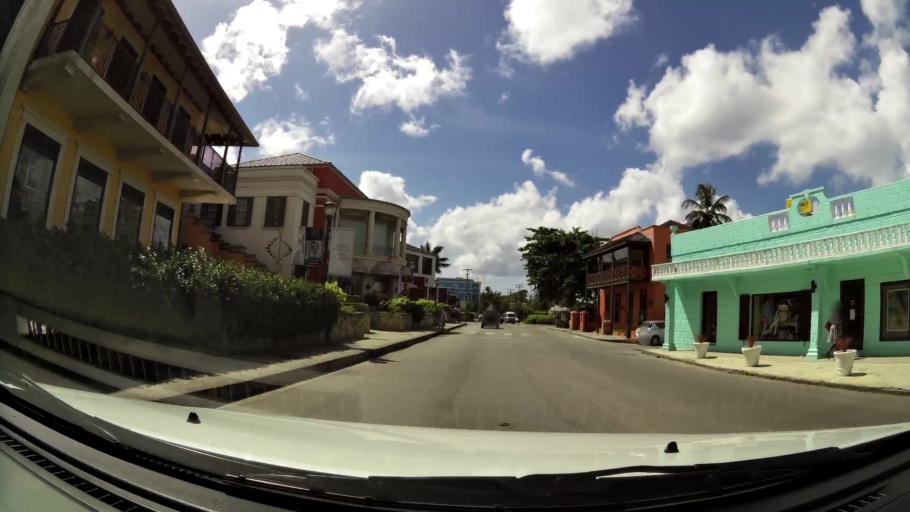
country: BB
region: Saint James
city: Holetown
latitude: 13.1870
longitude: -59.6363
